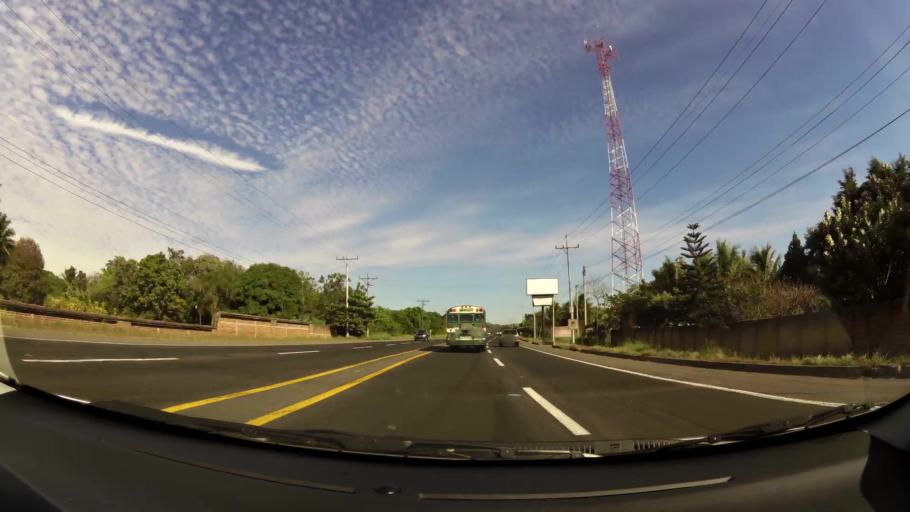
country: SV
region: Santa Ana
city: Santa Ana
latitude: 13.9887
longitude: -89.6203
